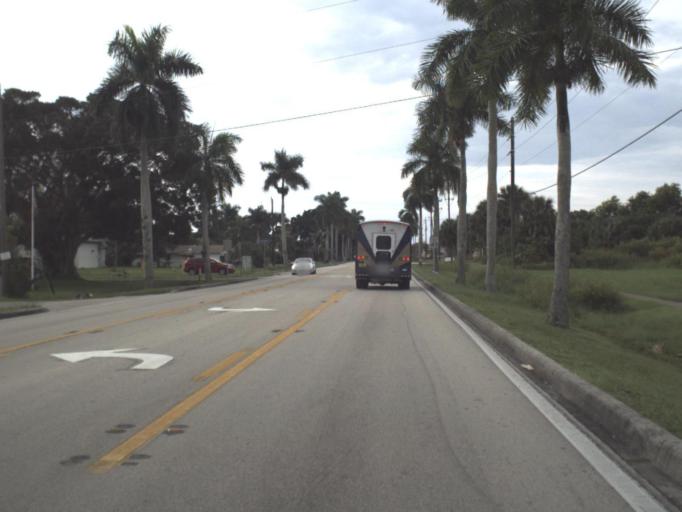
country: US
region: Florida
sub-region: Lee County
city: Harlem Heights
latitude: 26.5002
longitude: -81.9435
